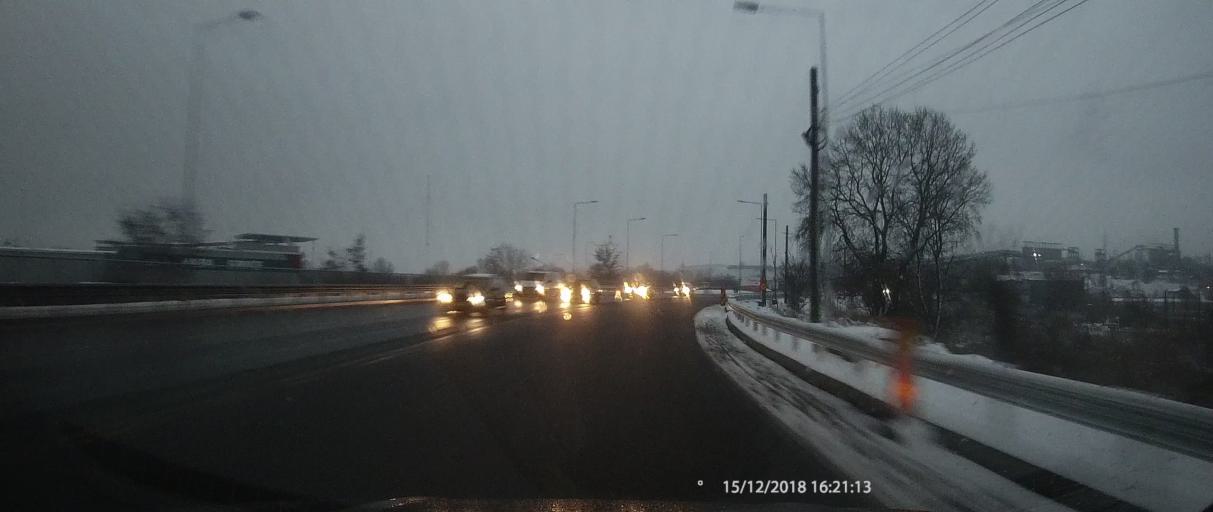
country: RO
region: Galati
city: Galati
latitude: 45.4088
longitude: 28.0005
